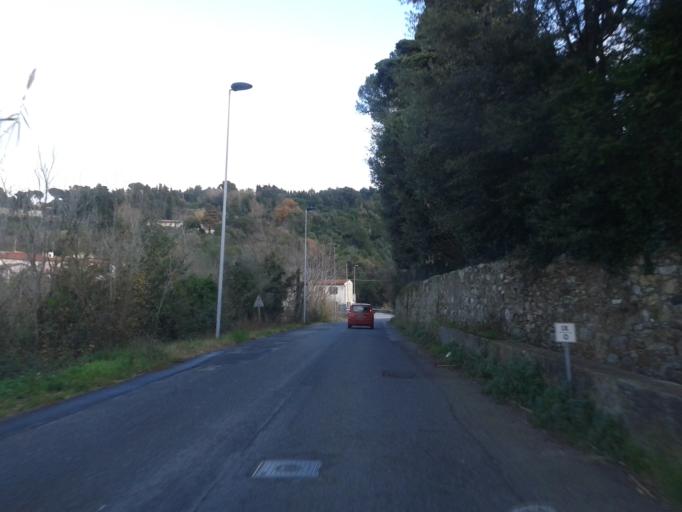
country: IT
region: Tuscany
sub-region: Provincia di Livorno
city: Quercianella
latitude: 43.4978
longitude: 10.3507
